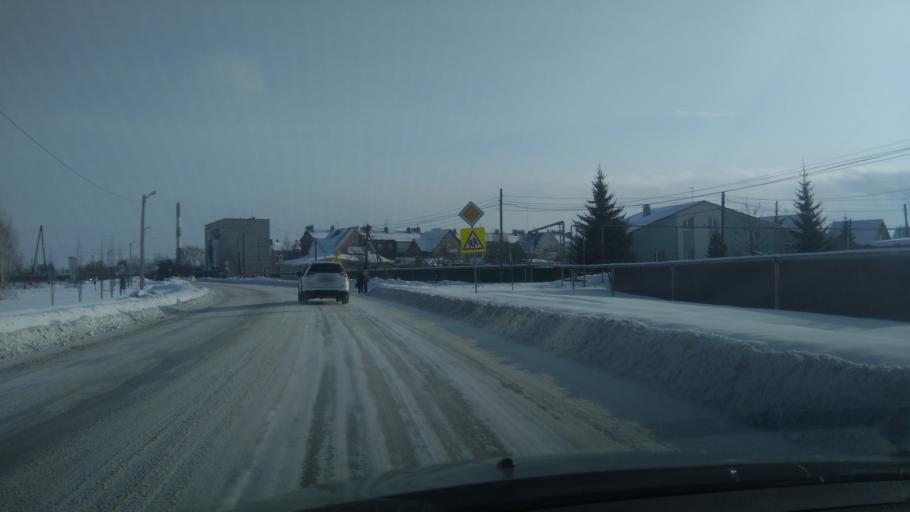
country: RU
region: Sverdlovsk
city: Sukhoy Log
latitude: 56.8912
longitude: 62.0371
